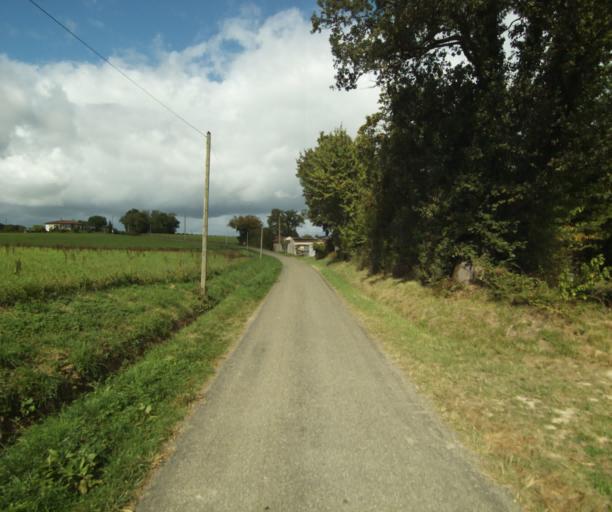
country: FR
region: Midi-Pyrenees
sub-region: Departement du Gers
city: Cazaubon
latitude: 43.8535
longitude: -0.0343
